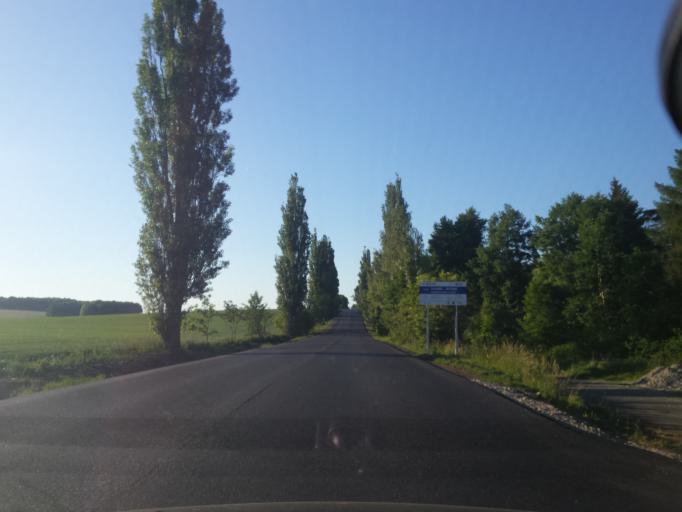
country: CZ
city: Duba
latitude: 50.5570
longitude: 14.5421
